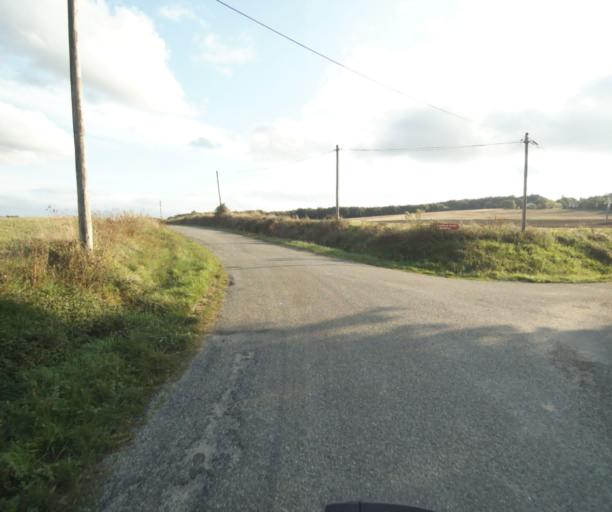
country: FR
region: Midi-Pyrenees
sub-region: Departement de la Haute-Garonne
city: Launac
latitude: 43.8170
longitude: 1.1358
